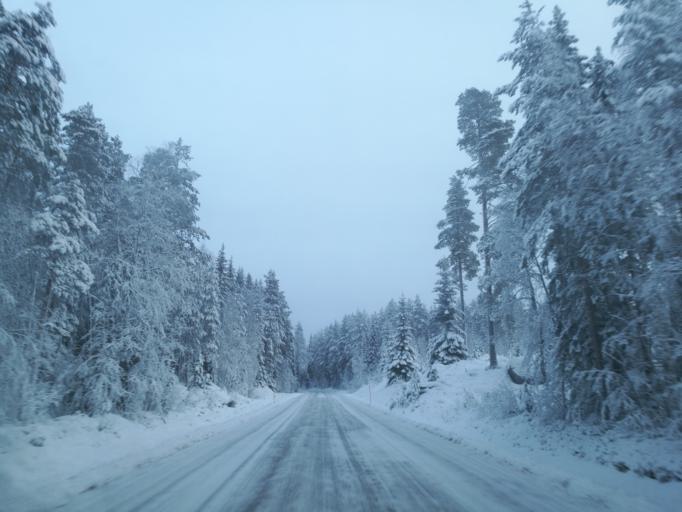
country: NO
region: Hedmark
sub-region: Grue
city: Kirkenaer
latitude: 60.4660
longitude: 12.5428
